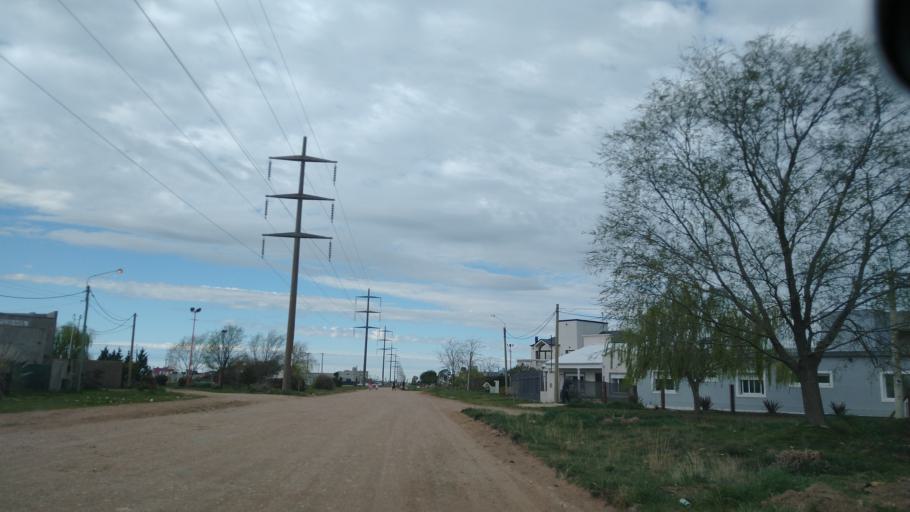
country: AR
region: Buenos Aires
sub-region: Partido de Bahia Blanca
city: Bahia Blanca
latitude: -38.7043
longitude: -62.2027
